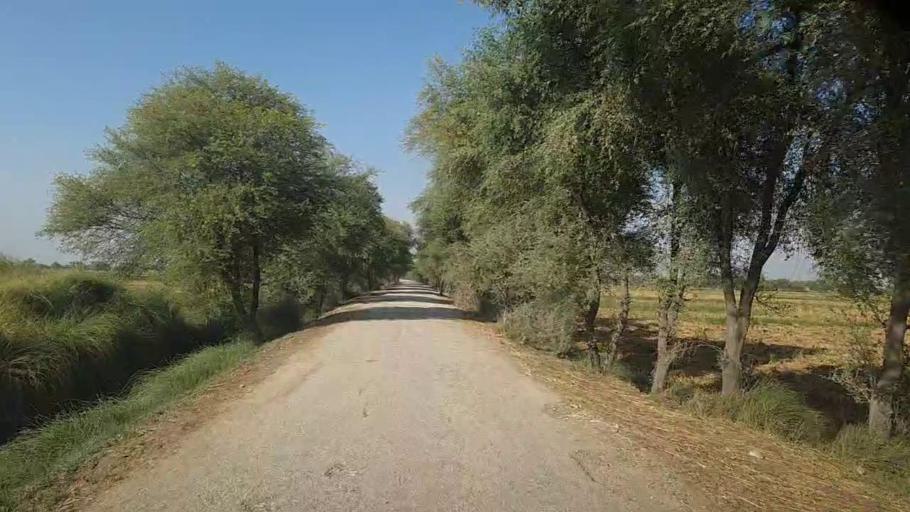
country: PK
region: Sindh
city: Tangwani
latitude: 28.2810
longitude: 68.9843
